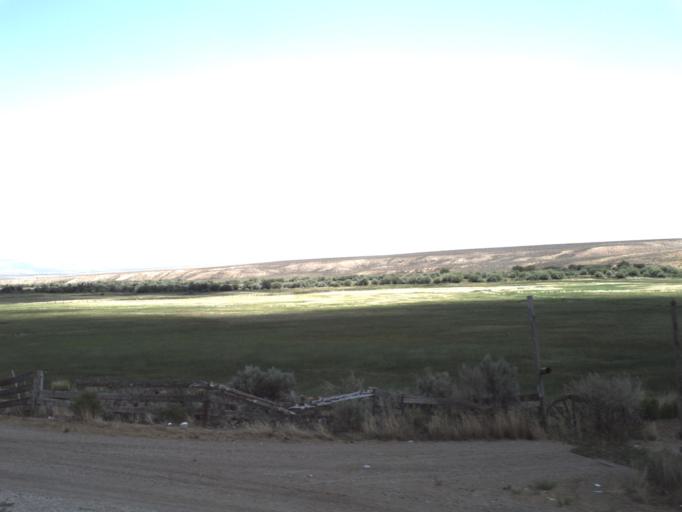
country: US
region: Utah
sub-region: Rich County
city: Randolph
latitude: 41.5202
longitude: -111.1984
